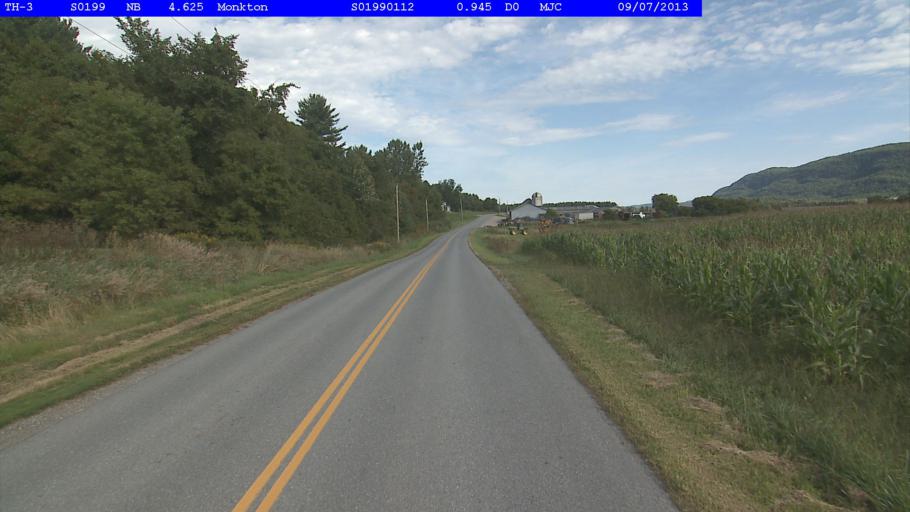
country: US
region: Vermont
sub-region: Addison County
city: Bristol
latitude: 44.1942
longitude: -73.1094
